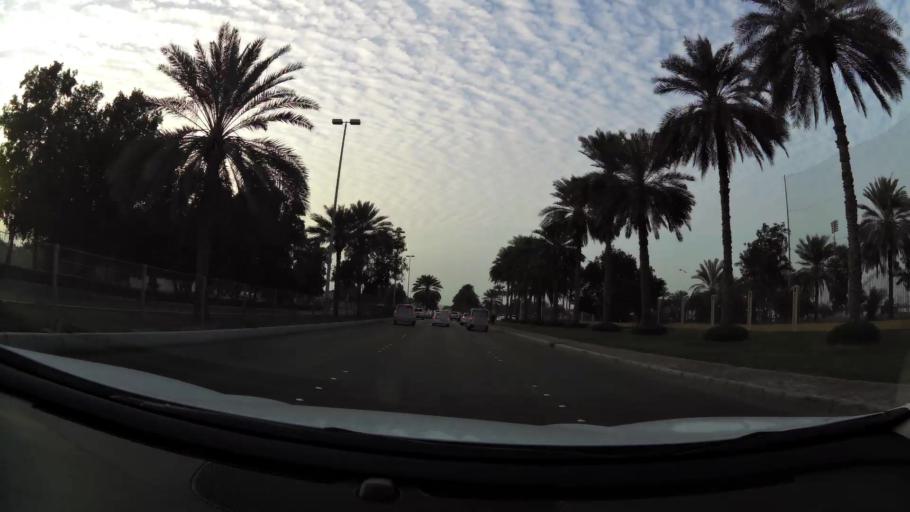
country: AE
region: Abu Dhabi
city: Abu Dhabi
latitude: 24.4412
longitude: 54.3757
